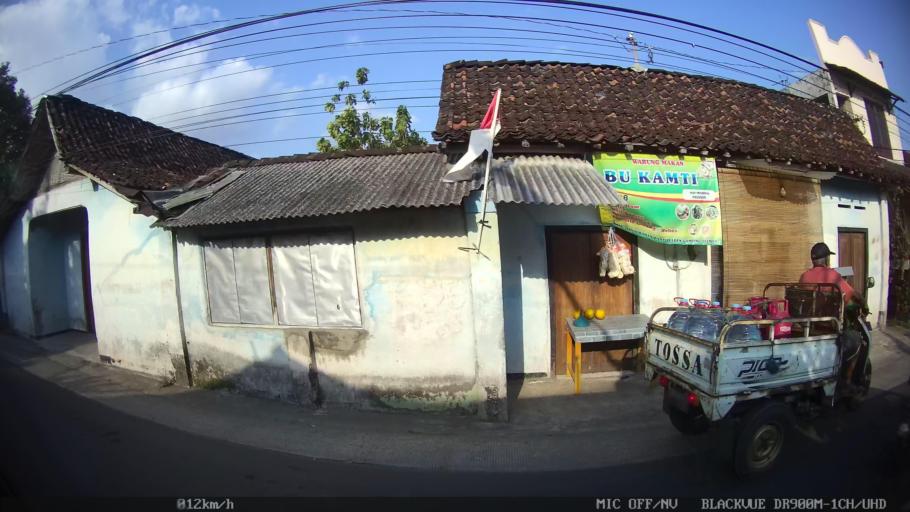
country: ID
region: Daerah Istimewa Yogyakarta
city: Gamping Lor
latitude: -7.7944
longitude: 110.3365
